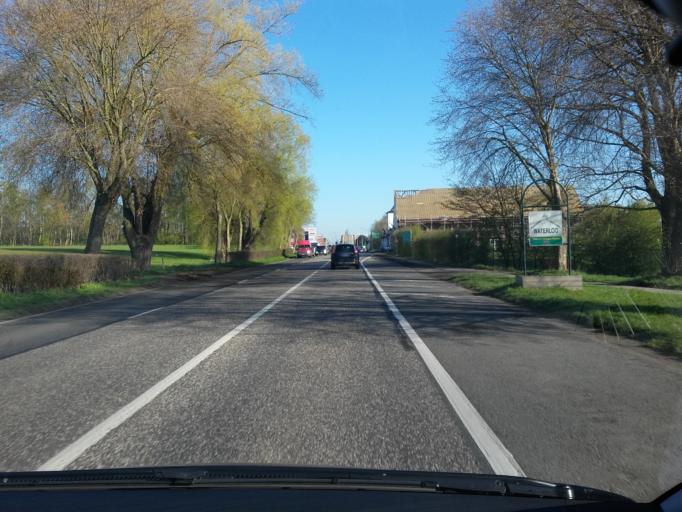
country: BE
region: Wallonia
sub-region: Province du Brabant Wallon
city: Waterloo
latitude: 50.6843
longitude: 4.4101
